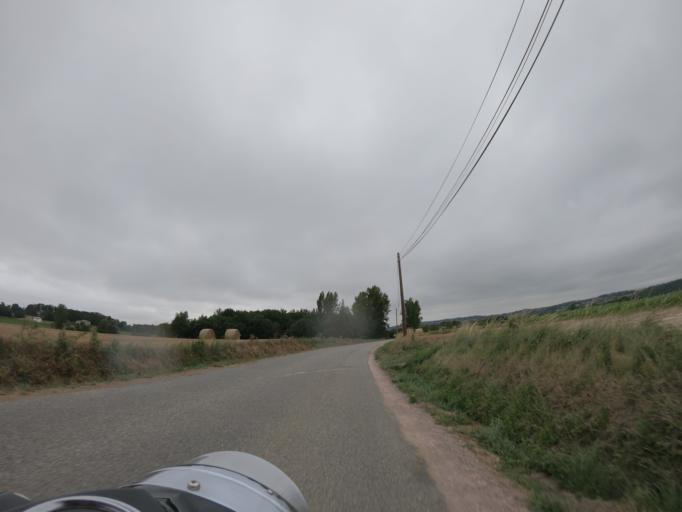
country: FR
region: Midi-Pyrenees
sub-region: Departement de l'Ariege
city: La Tour-du-Crieu
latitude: 43.1000
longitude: 1.7211
